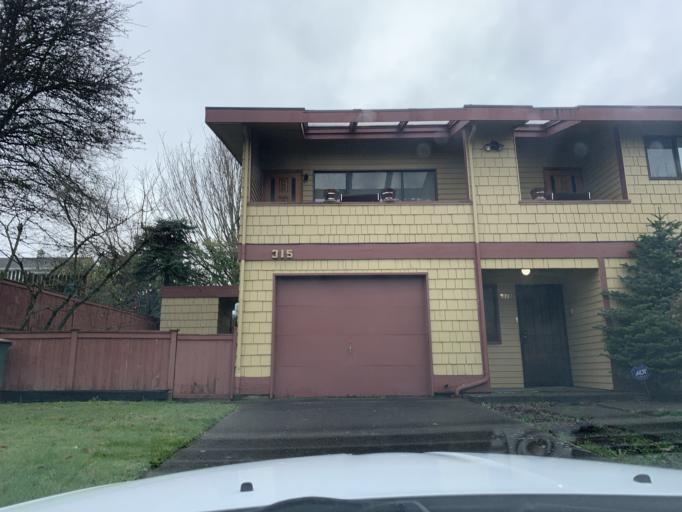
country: US
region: Washington
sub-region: King County
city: Seattle
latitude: 47.6047
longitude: -122.2927
